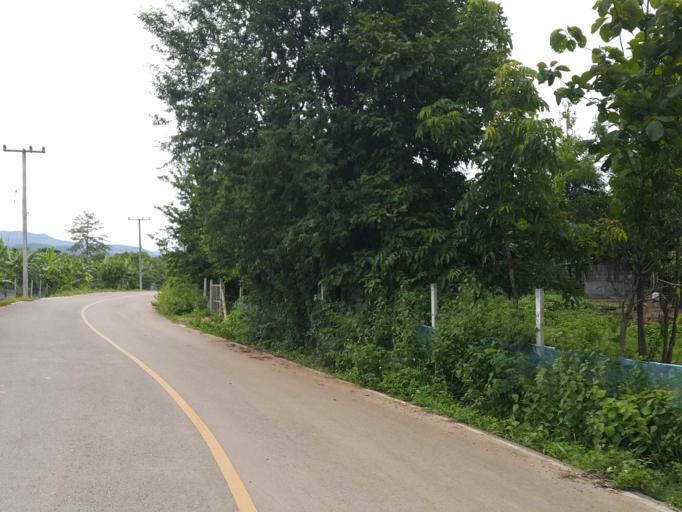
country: TH
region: Chiang Mai
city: San Sai
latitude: 18.9469
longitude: 98.9162
